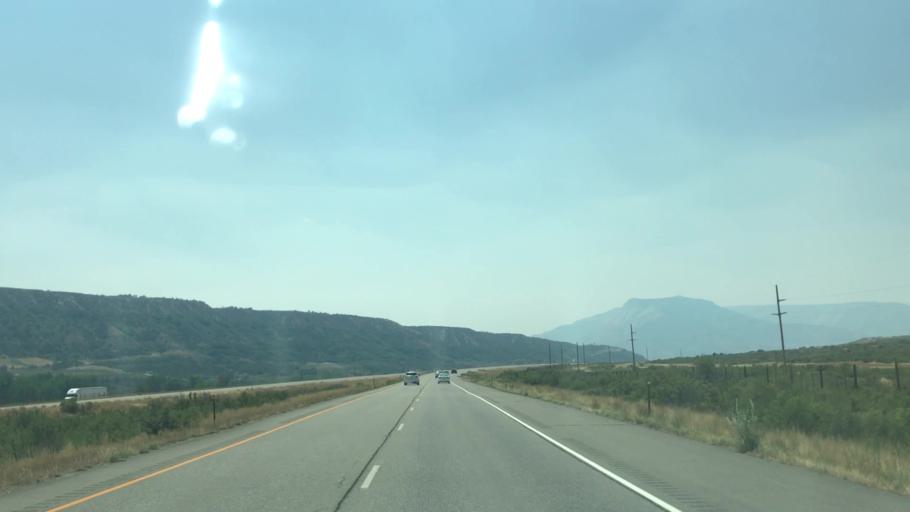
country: US
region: Colorado
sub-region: Garfield County
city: Battlement Mesa
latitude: 39.4812
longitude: -107.9703
